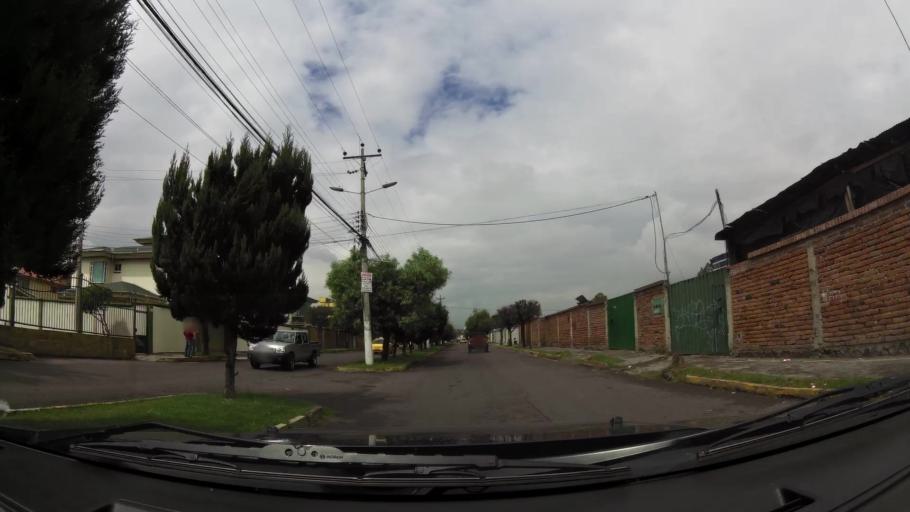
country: EC
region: Pichincha
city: Sangolqui
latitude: -0.3062
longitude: -78.4704
